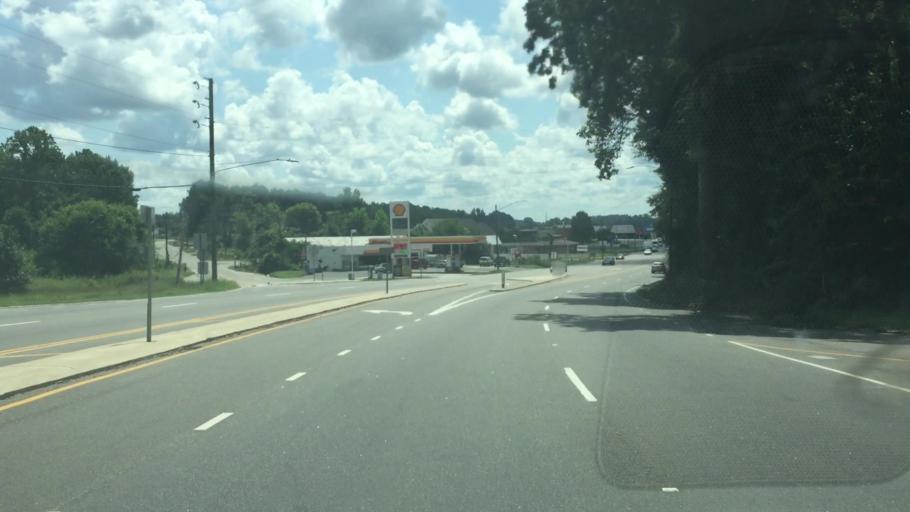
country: US
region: North Carolina
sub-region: Anson County
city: Wadesboro
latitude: 34.9694
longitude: -80.0669
